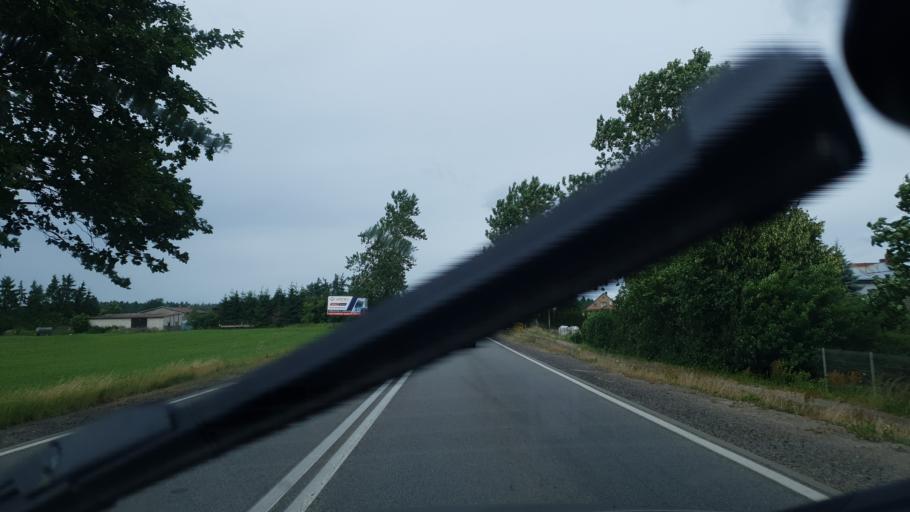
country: PL
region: Pomeranian Voivodeship
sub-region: Powiat kartuski
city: Chwaszczyno
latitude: 54.4254
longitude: 18.3858
